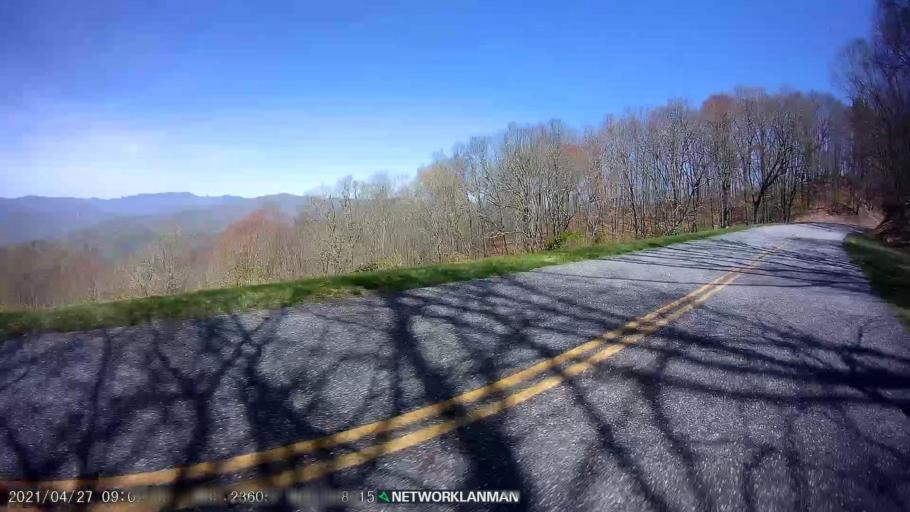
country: US
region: North Carolina
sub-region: Swain County
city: Cherokee
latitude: 35.5289
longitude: -83.2356
